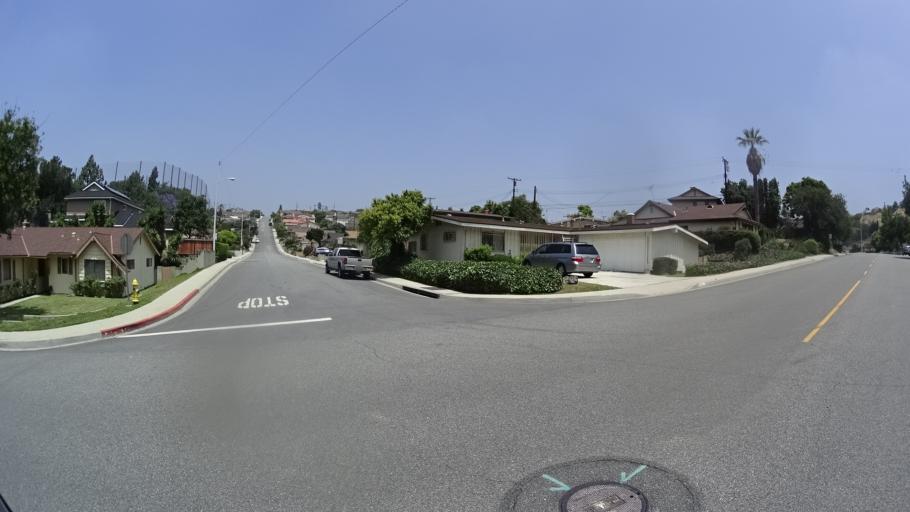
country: US
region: California
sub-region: Los Angeles County
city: Belvedere
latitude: 34.0555
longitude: -118.1601
